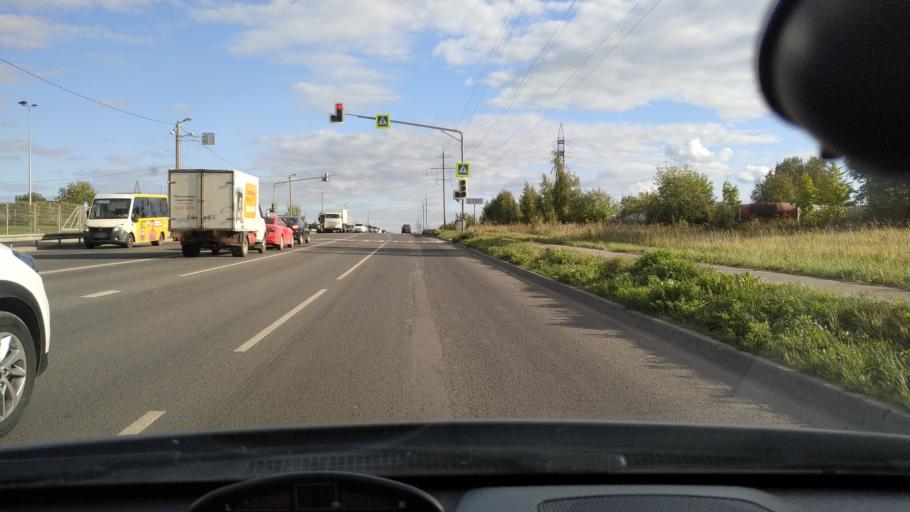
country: RU
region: Rjazan
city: Ryazan'
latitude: 54.5908
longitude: 39.8138
